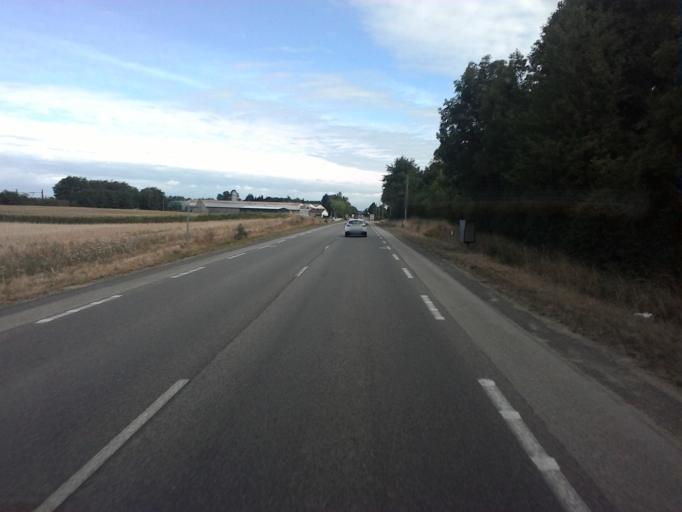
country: FR
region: Rhone-Alpes
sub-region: Departement de l'Ain
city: Tossiat
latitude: 46.1292
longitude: 5.2915
